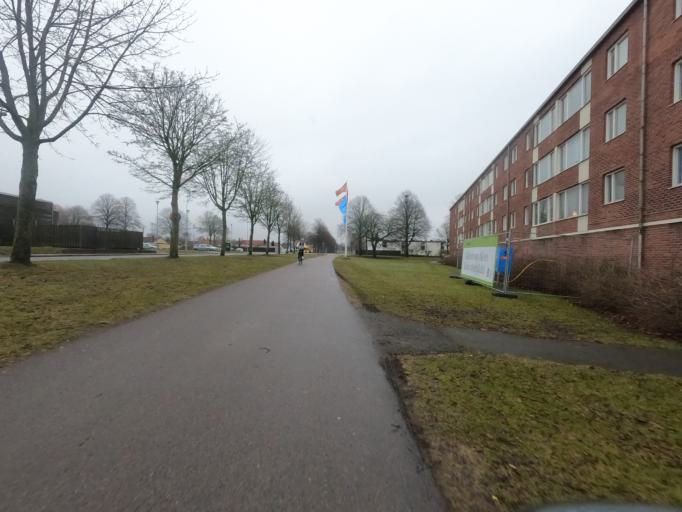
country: SE
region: Halland
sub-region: Halmstads Kommun
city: Fyllinge
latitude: 56.6722
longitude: 12.8911
